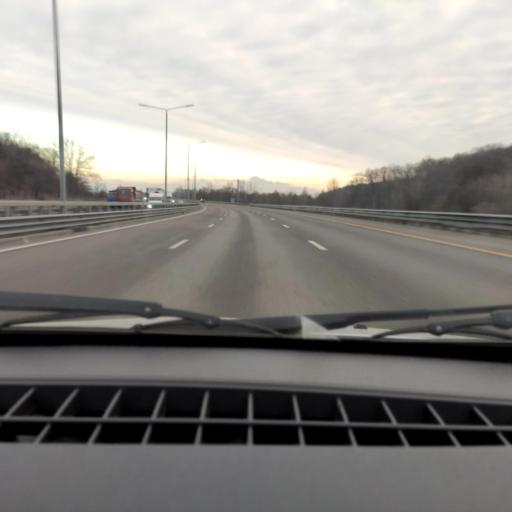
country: RU
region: Voronezj
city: Podgornoye
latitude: 51.7995
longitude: 39.2553
